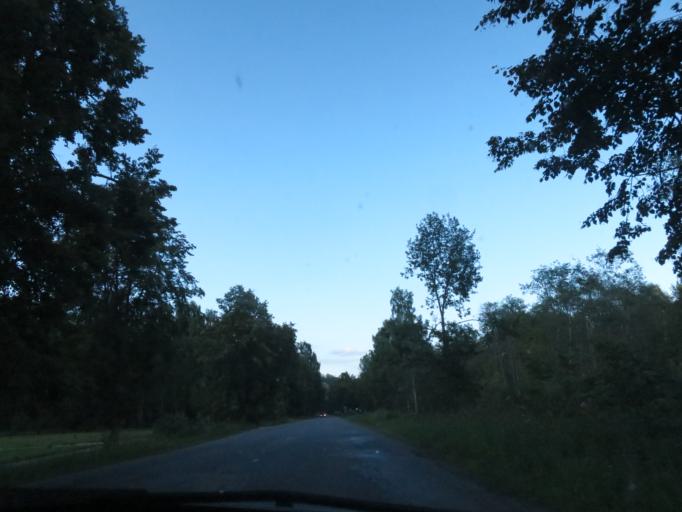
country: LV
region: Sigulda
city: Sigulda
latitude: 57.1749
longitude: 24.8440
